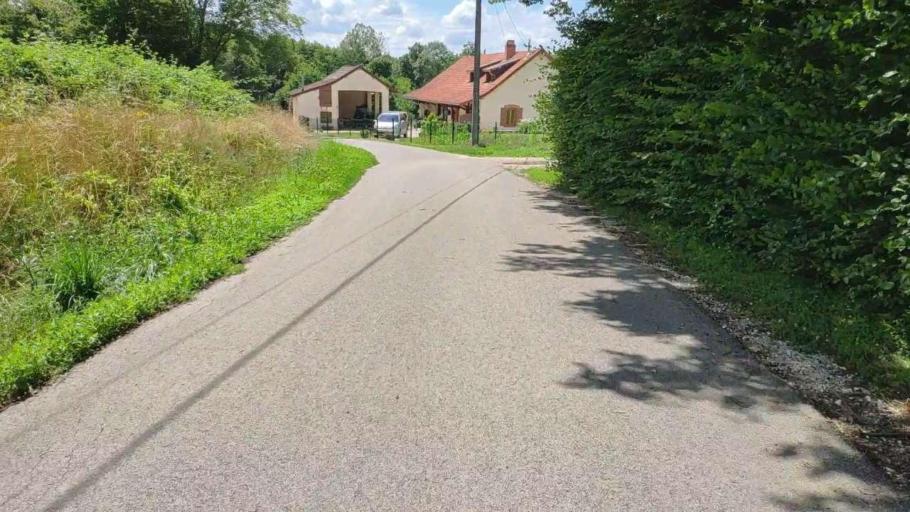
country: FR
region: Franche-Comte
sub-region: Departement du Jura
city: Bletterans
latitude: 46.8455
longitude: 5.4599
